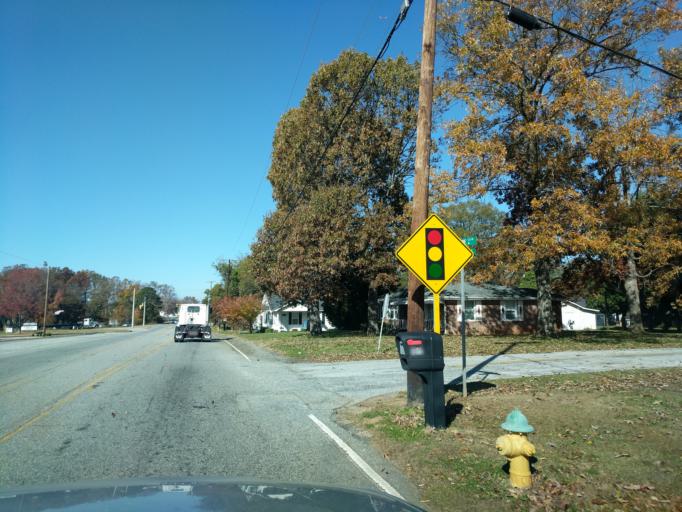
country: US
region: South Carolina
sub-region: Greenville County
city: Greer
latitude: 34.9110
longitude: -82.2353
